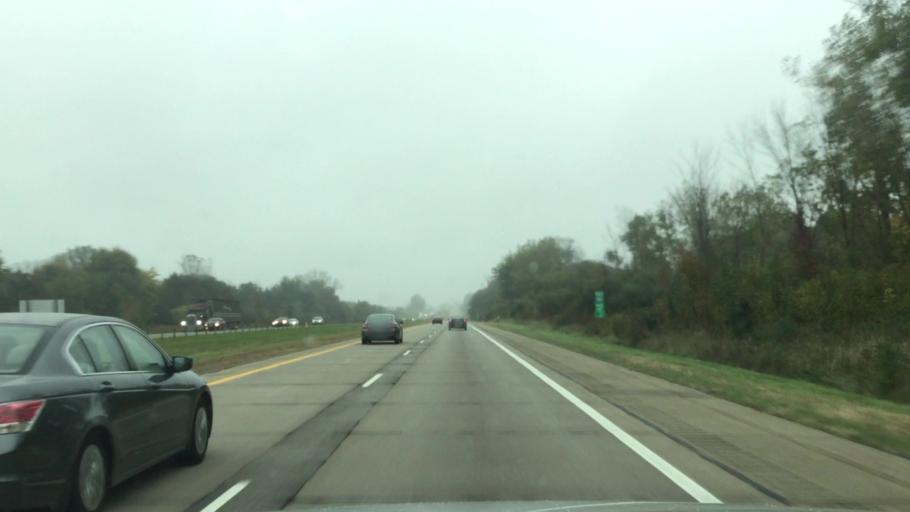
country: US
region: Michigan
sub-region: Van Buren County
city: Hartford
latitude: 42.1936
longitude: -86.1395
